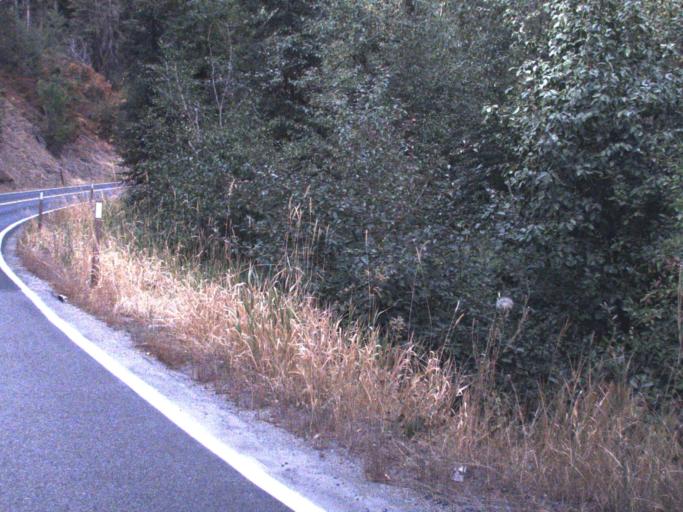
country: US
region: Washington
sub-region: Spokane County
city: Trentwood
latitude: 47.8476
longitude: -117.1686
